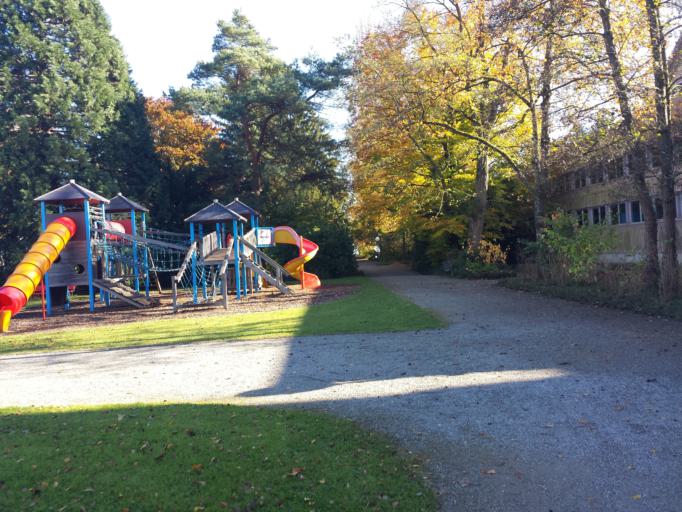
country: CH
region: Thurgau
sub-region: Arbon District
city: Romanshorn
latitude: 47.5722
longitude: 9.3795
